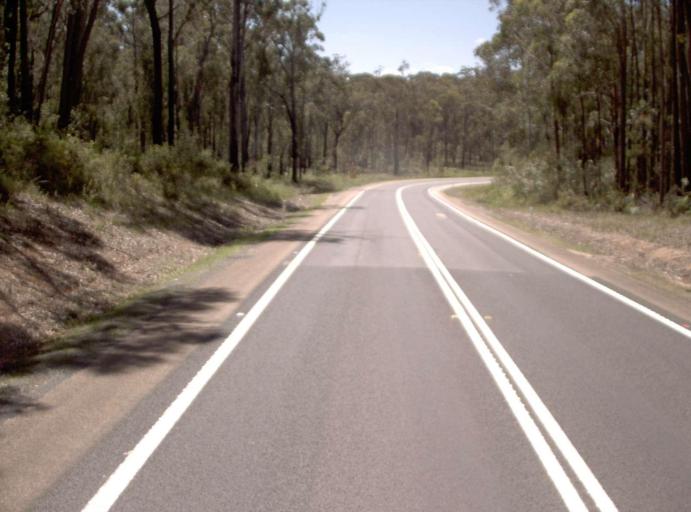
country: AU
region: Victoria
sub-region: East Gippsland
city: Lakes Entrance
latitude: -37.6905
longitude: 148.7499
